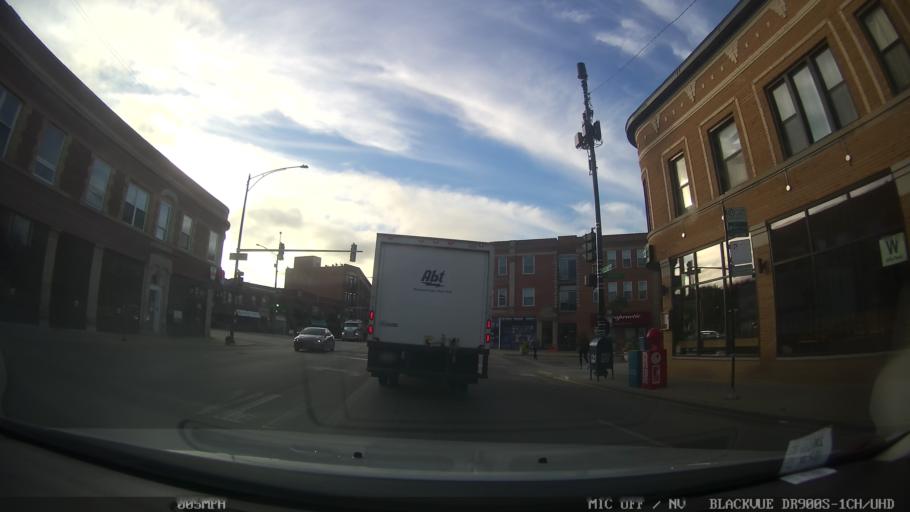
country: US
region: Illinois
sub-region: Cook County
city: Lincolnwood
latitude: 41.9513
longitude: -87.6598
